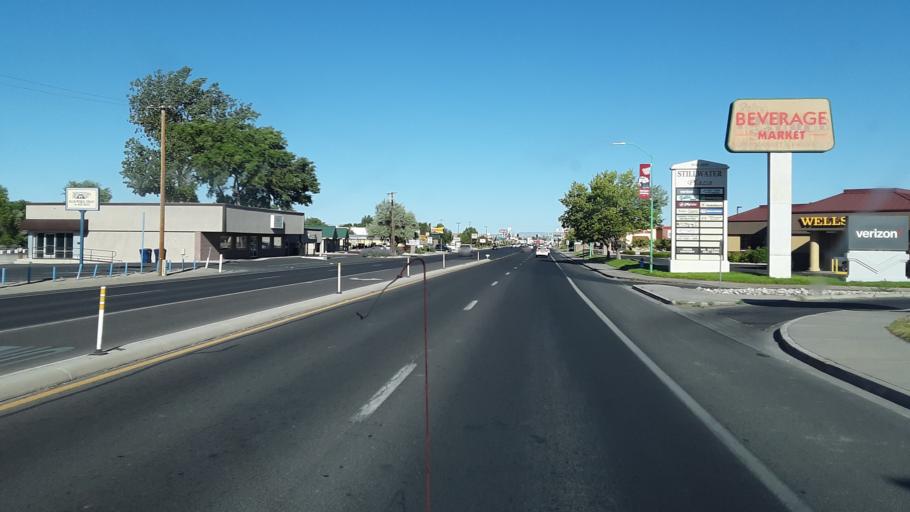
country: US
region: Nevada
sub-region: Churchill County
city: Fallon
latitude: 39.4773
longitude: -118.8048
